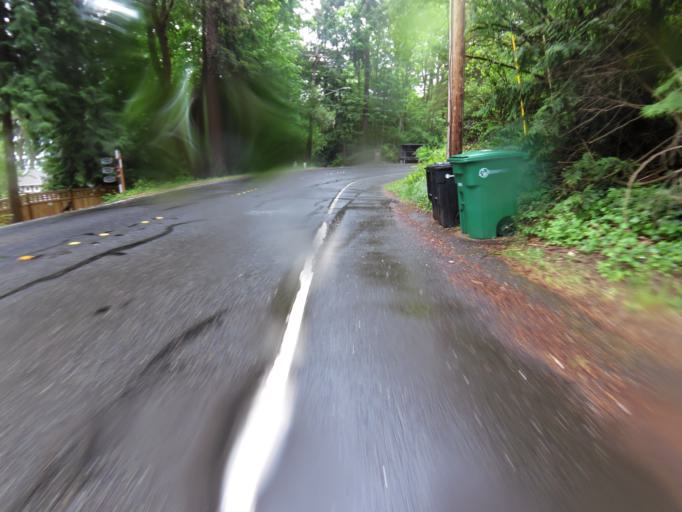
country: US
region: Washington
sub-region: King County
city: Mercer Island
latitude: 47.5453
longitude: -122.2121
